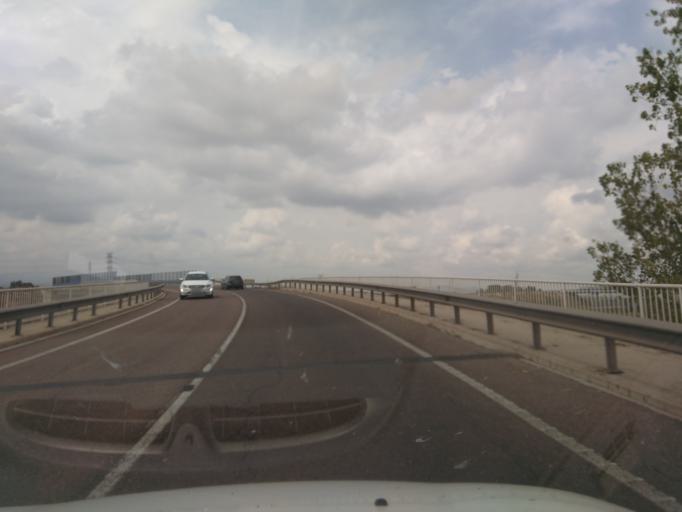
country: ES
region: Valencia
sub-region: Provincia de Valencia
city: Alzira
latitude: 39.1603
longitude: -0.4488
